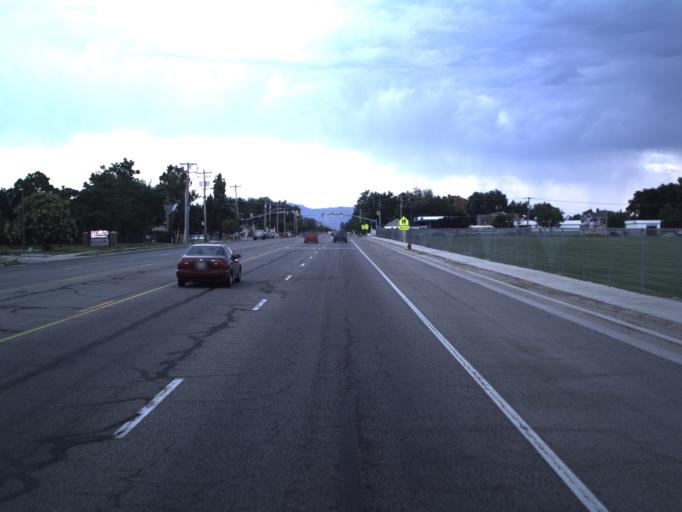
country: US
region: Utah
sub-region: Salt Lake County
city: Sandy City
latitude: 40.6081
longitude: -111.8723
